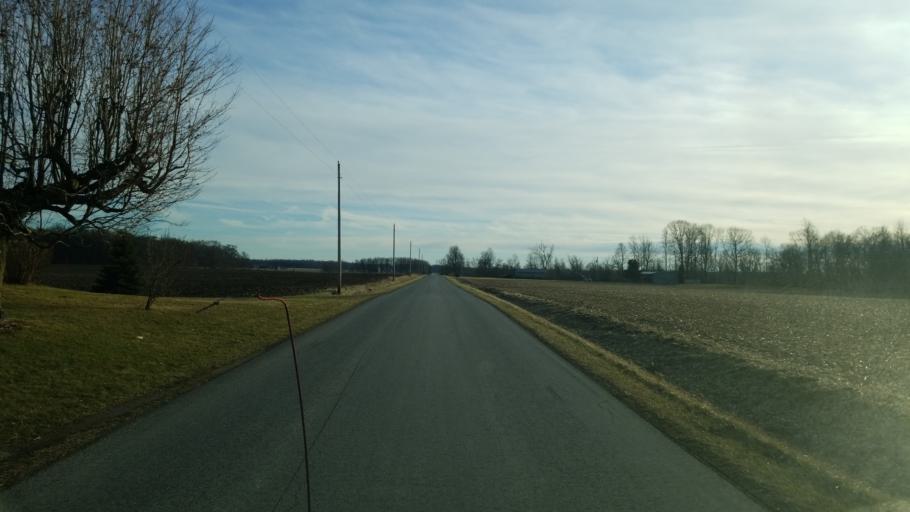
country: US
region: Ohio
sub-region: Huron County
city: Greenwich
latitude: 41.0052
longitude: -82.5346
